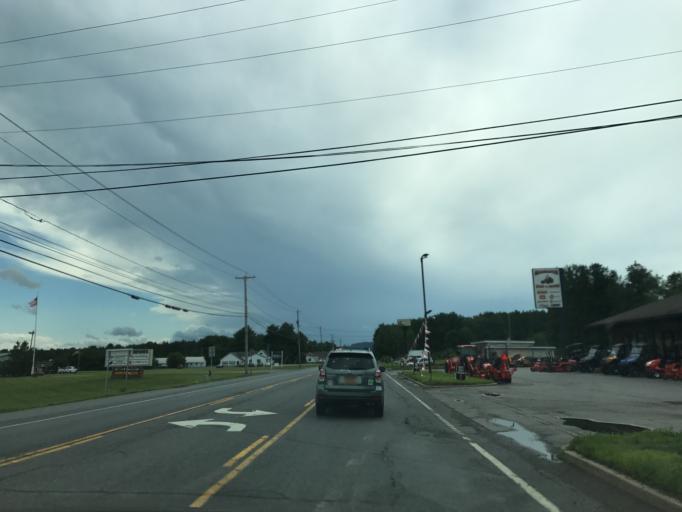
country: US
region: New York
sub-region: Warren County
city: West Glens Falls
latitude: 43.2494
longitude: -73.6720
